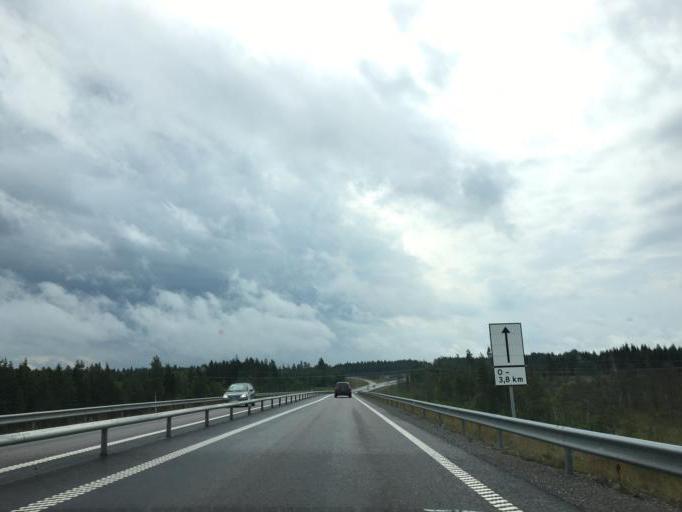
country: SE
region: Soedermanland
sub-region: Katrineholms Kommun
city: Katrineholm
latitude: 58.9993
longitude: 16.2521
